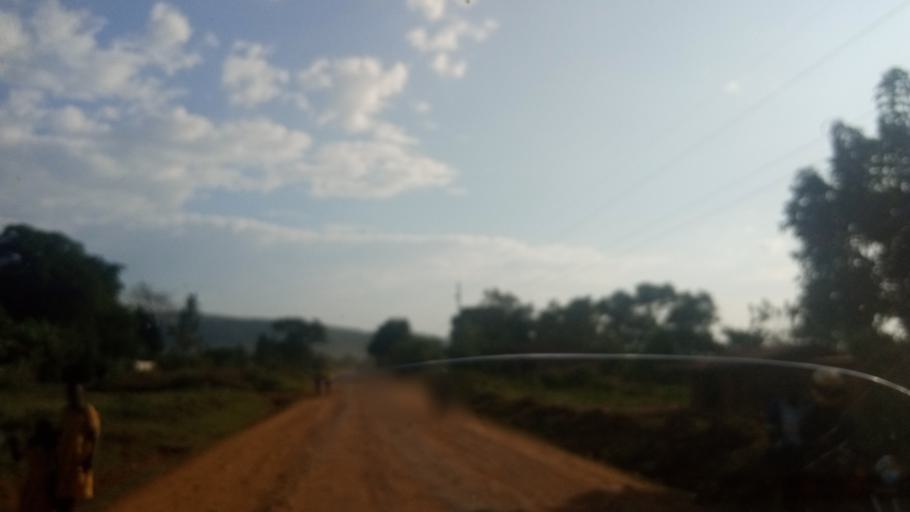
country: UG
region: Eastern Region
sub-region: Kapchorwa District
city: Kapchorwa
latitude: 1.4131
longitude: 34.3490
